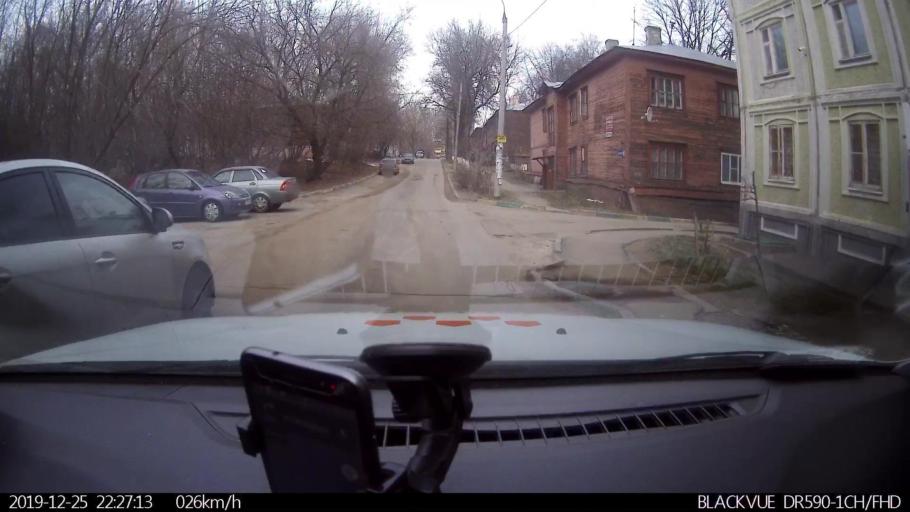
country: RU
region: Nizjnij Novgorod
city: Nizhniy Novgorod
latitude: 56.2628
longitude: 43.9759
